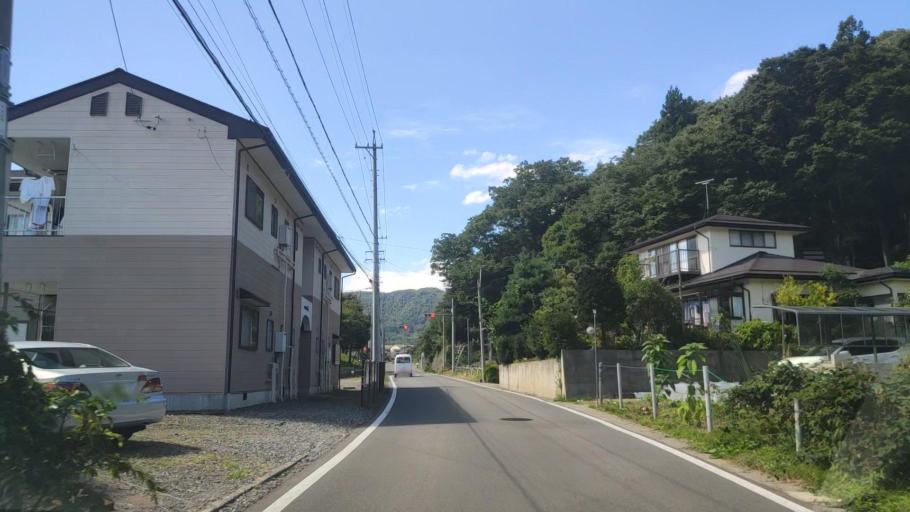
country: JP
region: Nagano
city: Nagano-shi
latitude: 36.6881
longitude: 138.2139
